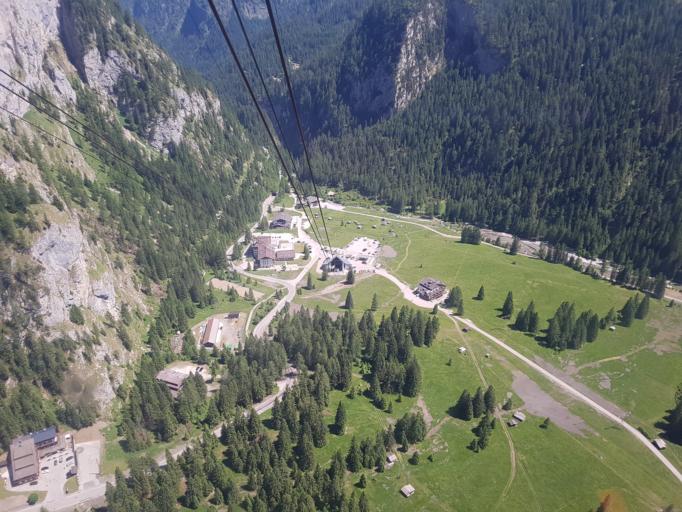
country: IT
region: Veneto
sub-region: Provincia di Belluno
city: Sachet
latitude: 46.4306
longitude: 11.9047
